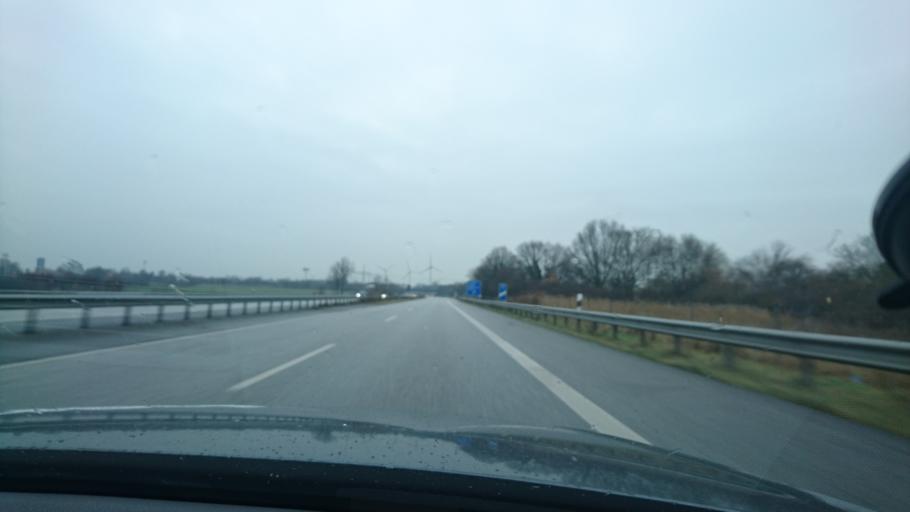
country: DE
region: Schleswig-Holstein
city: Kabelhorst
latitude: 54.2102
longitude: 10.9009
